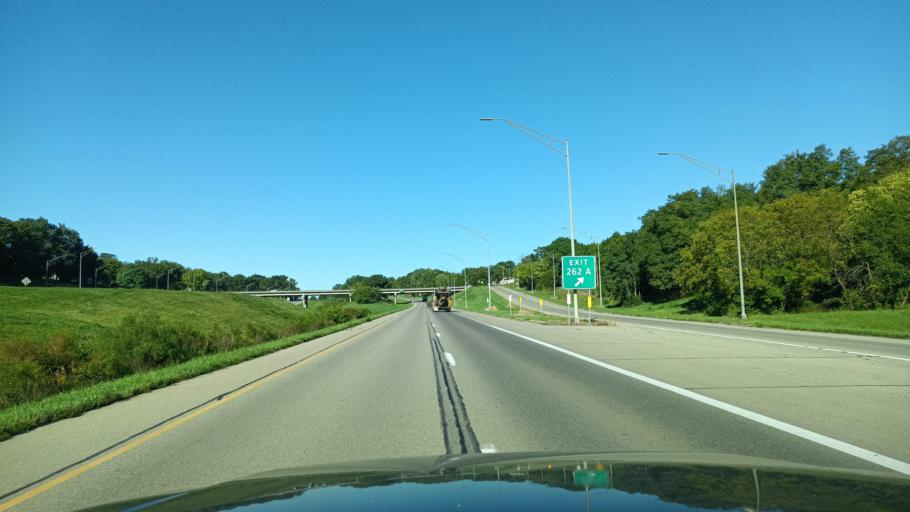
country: US
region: Iowa
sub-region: Des Moines County
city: Burlington
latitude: 40.8174
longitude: -91.1217
